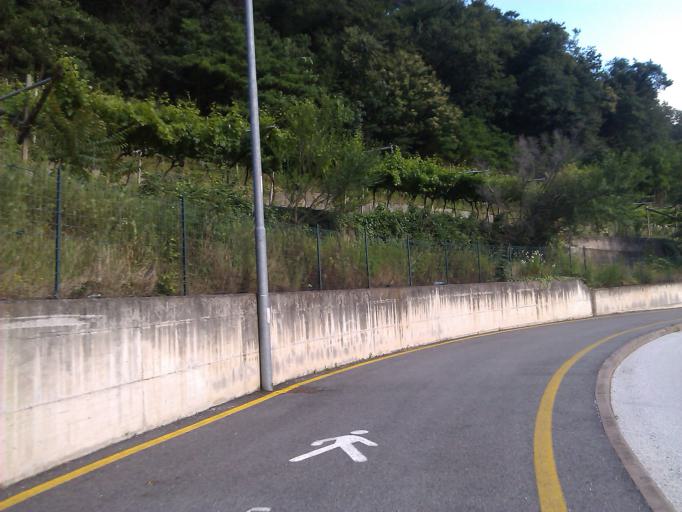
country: IT
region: Trentino-Alto Adige
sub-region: Provincia di Trento
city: Meano
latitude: 46.1330
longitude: 11.1139
